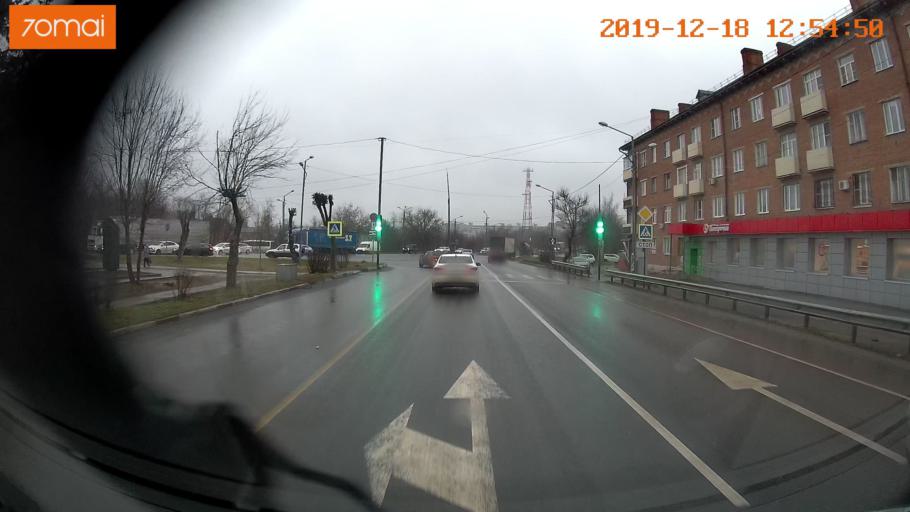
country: RU
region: Moskovskaya
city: Klin
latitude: 56.3273
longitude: 36.7057
